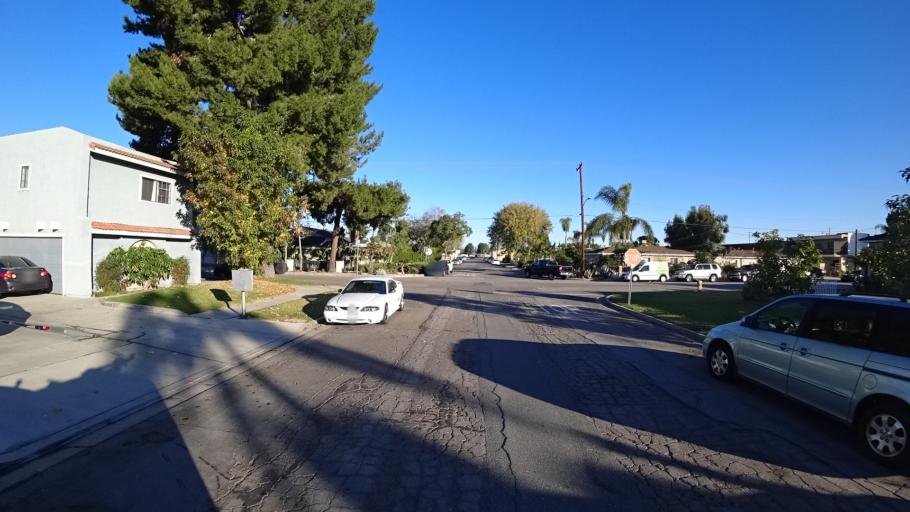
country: US
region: California
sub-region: Orange County
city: Westminster
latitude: 33.7718
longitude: -117.9834
